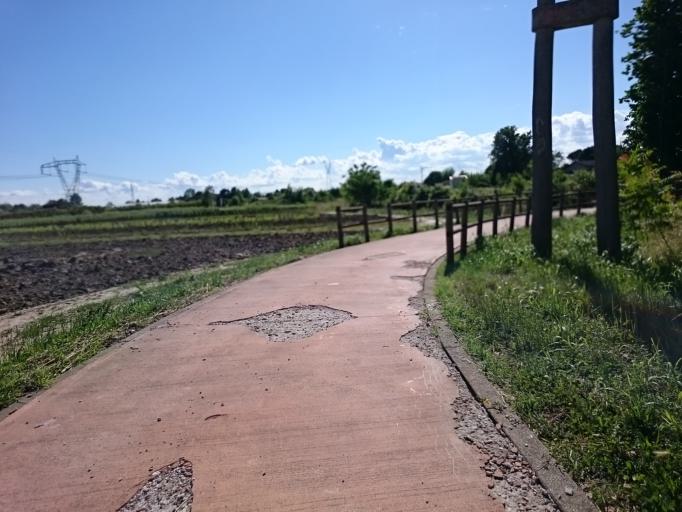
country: IT
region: Veneto
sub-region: Provincia di Padova
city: Saonara
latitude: 45.3607
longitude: 11.9903
